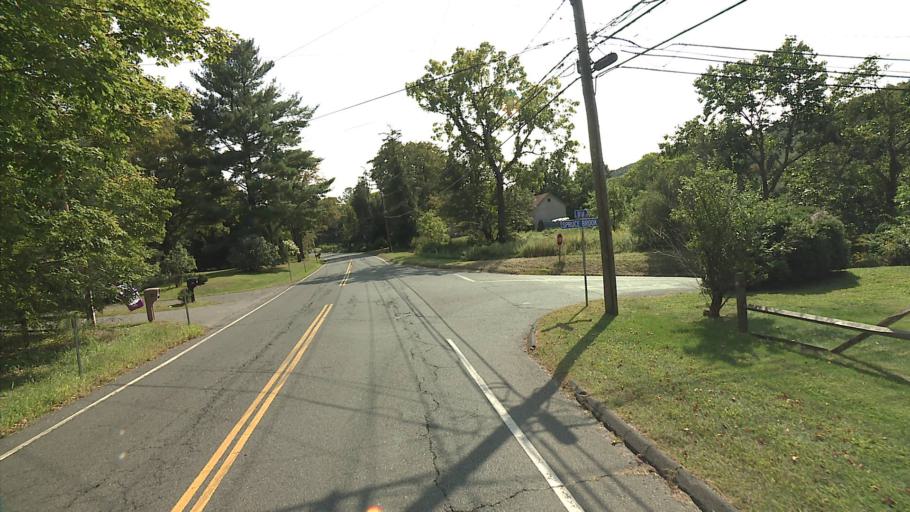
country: US
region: Connecticut
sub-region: New Haven County
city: Heritage Village
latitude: 41.4833
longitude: -73.2577
